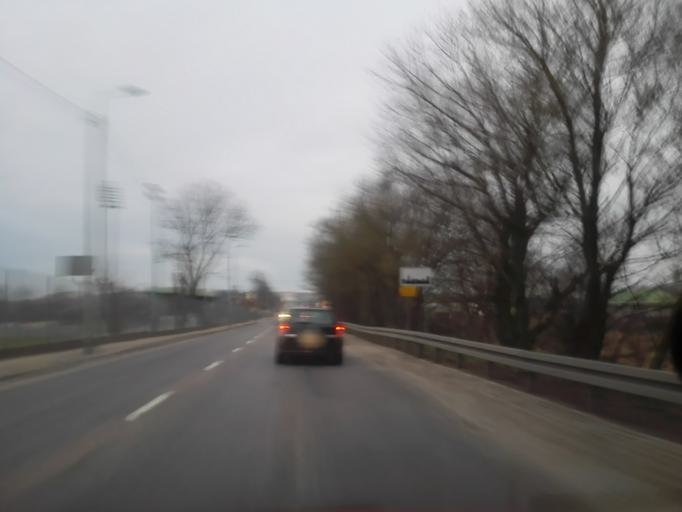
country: PL
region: Podlasie
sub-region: Powiat lomzynski
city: Piatnica
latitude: 53.1889
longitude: 22.0887
